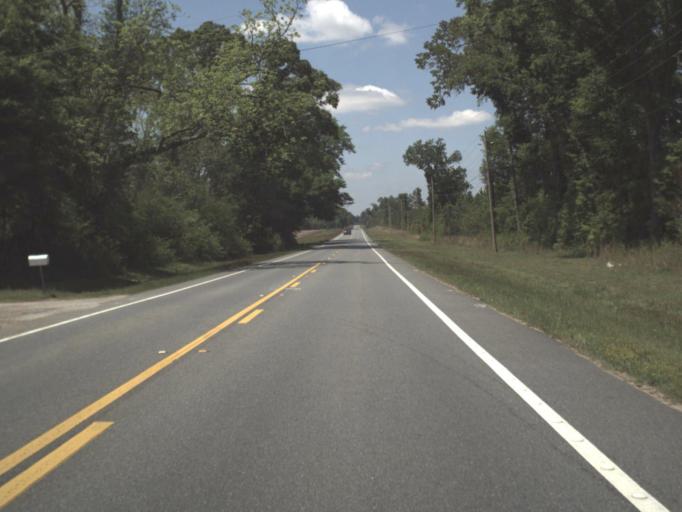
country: US
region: Alabama
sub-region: Escambia County
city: East Brewton
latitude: 30.9429
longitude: -87.0303
